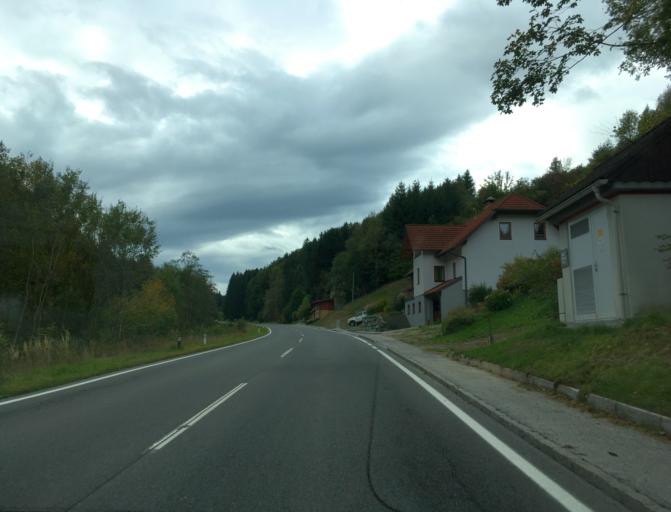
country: AT
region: Lower Austria
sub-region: Politischer Bezirk Neunkirchen
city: Thomasberg
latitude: 47.5641
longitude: 16.1424
